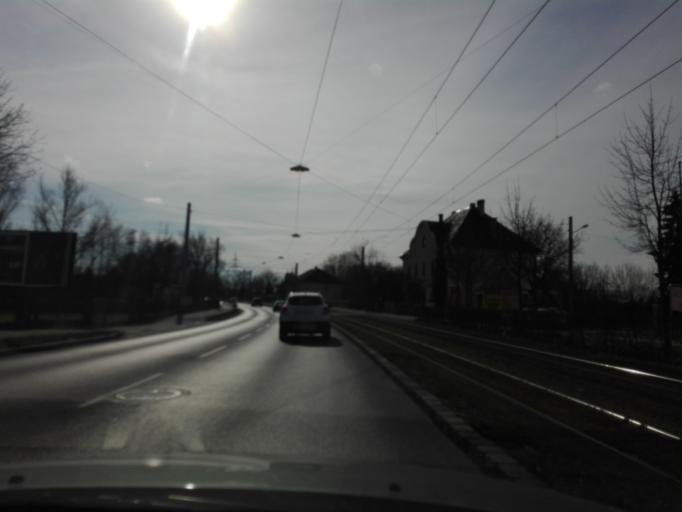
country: AT
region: Upper Austria
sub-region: Politischer Bezirk Linz-Land
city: Ansfelden
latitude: 48.2506
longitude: 14.3227
